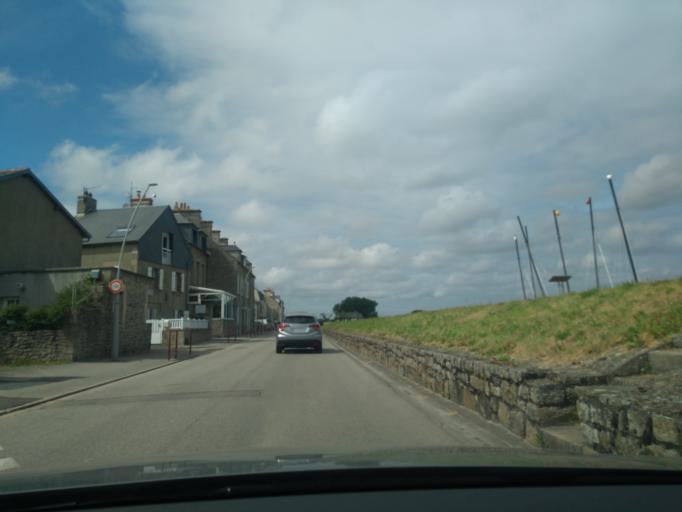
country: FR
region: Lower Normandy
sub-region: Departement de la Manche
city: Saint-Vaast-la-Hougue
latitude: 49.5901
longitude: -1.2665
